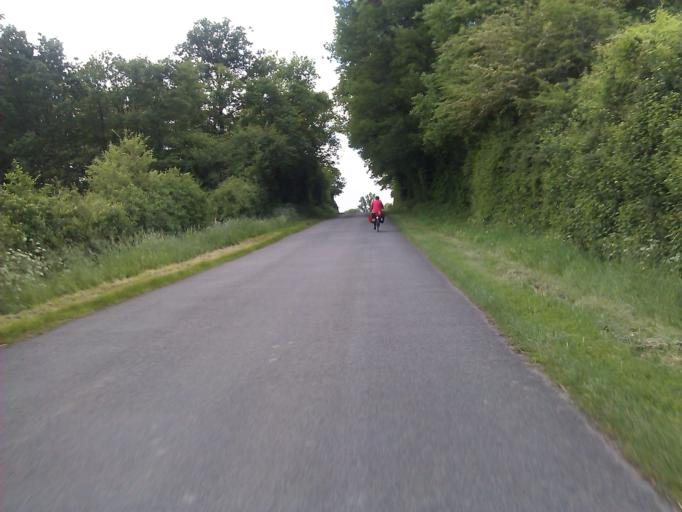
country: FR
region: Poitou-Charentes
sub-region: Departement de la Charente
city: Champagne-Mouton
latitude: 46.0157
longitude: 0.4340
